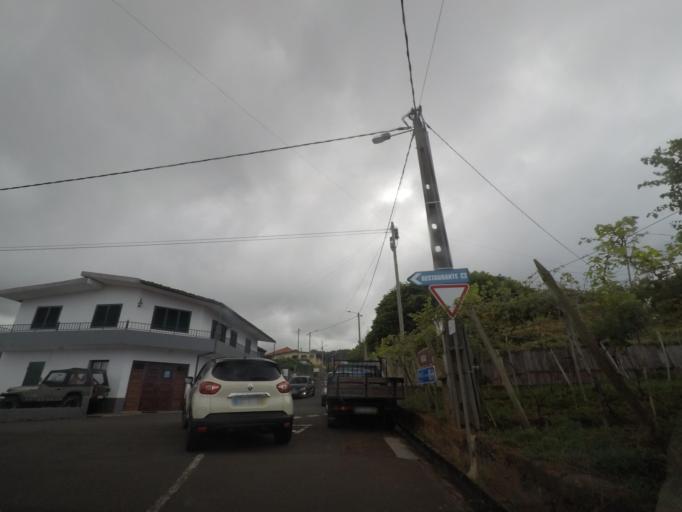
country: PT
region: Madeira
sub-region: Santana
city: Santana
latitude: 32.8322
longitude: -16.9086
